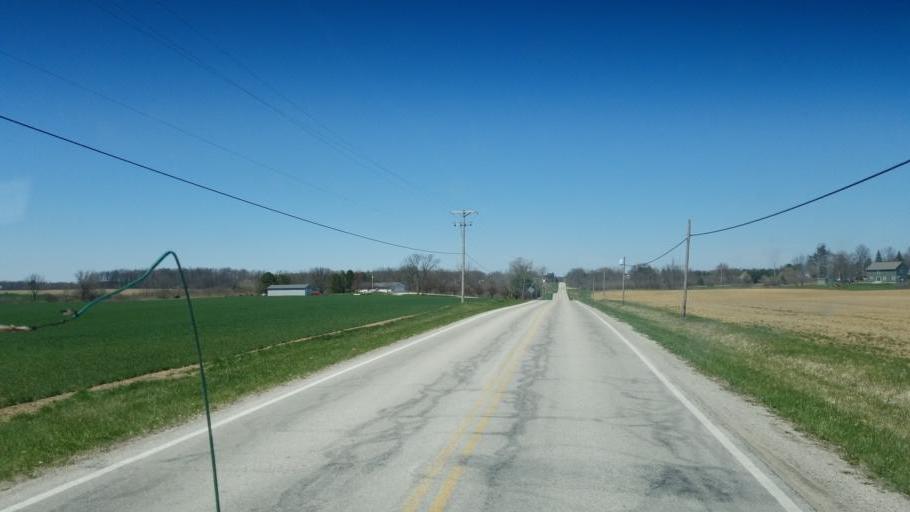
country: US
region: Ohio
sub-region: Huron County
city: Willard
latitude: 41.0832
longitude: -82.7412
